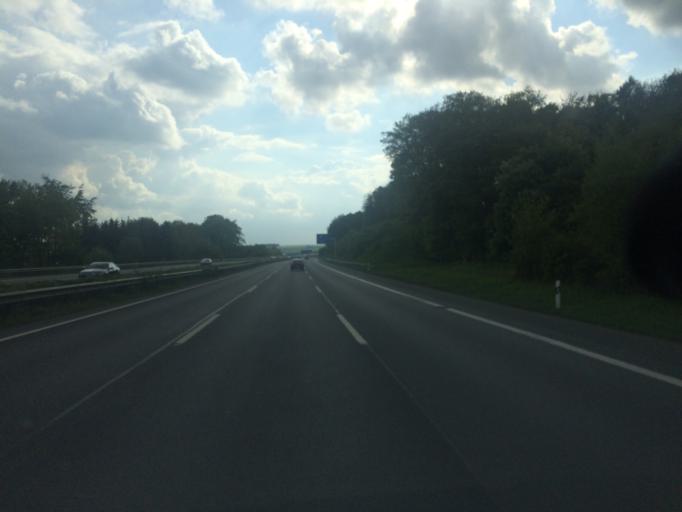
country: DE
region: North Rhine-Westphalia
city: Bad Oeynhausen
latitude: 52.1491
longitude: 8.8009
